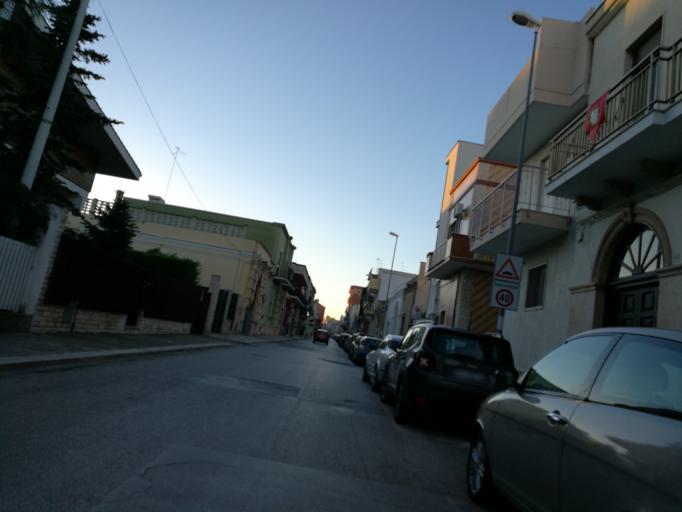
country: IT
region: Apulia
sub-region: Provincia di Bari
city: Adelfia
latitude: 41.0042
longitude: 16.8800
